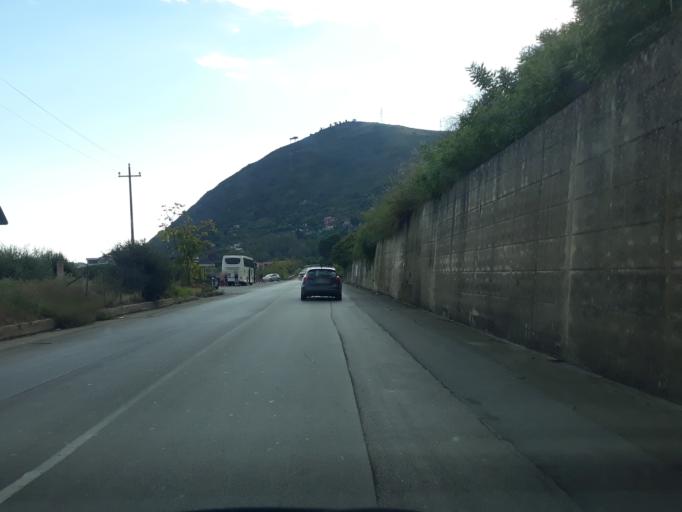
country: IT
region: Sicily
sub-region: Palermo
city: Cefalu
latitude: 38.0277
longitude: 14.0080
